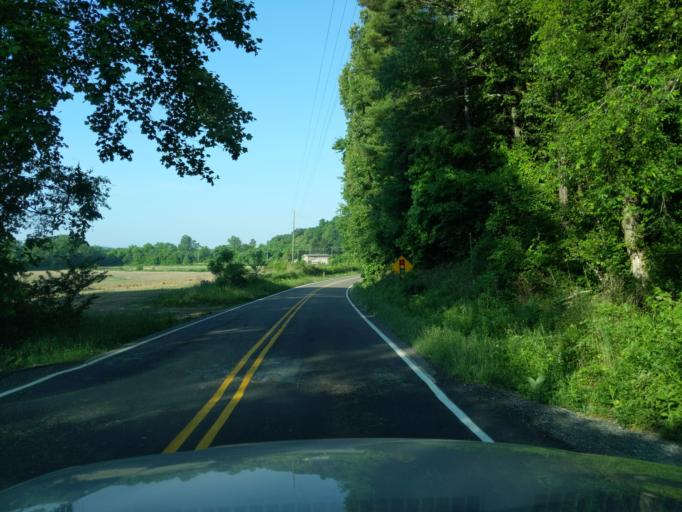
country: US
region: North Carolina
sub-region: Henderson County
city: Hoopers Creek
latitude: 35.4550
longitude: -82.4748
